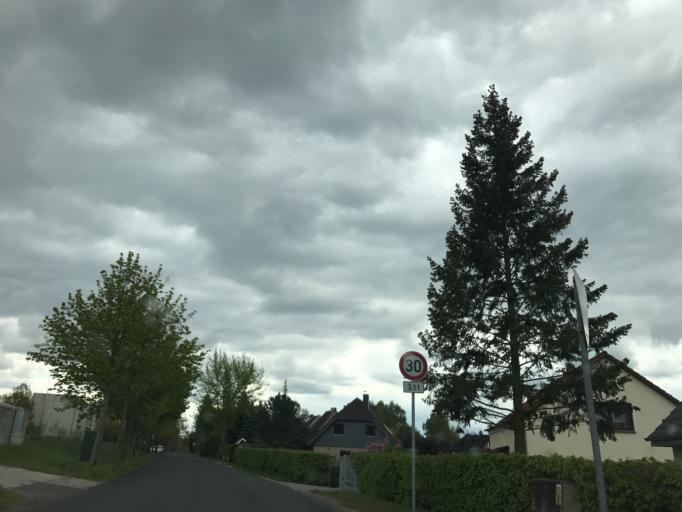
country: DE
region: Brandenburg
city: Wustermark
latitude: 52.4749
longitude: 12.9971
